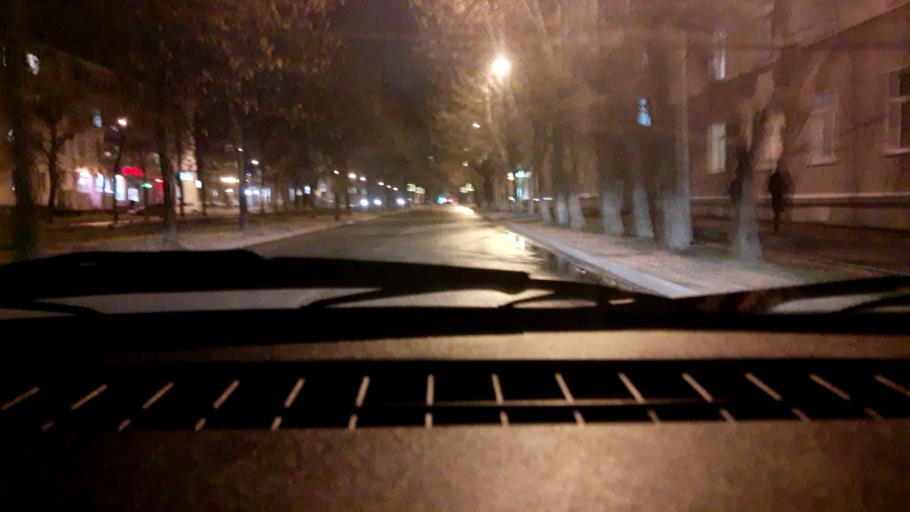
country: RU
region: Bashkortostan
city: Ufa
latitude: 54.8192
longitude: 56.0638
